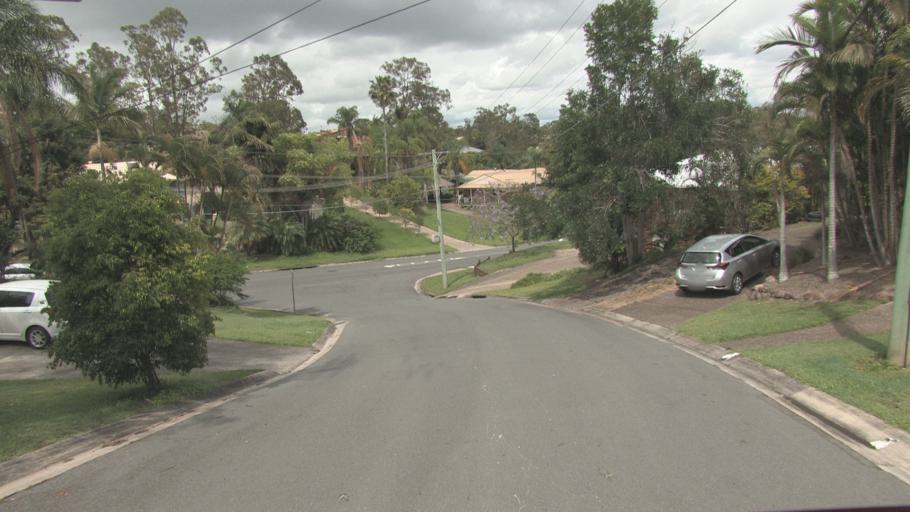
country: AU
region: Queensland
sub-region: Logan
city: Slacks Creek
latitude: -27.6493
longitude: 153.1809
